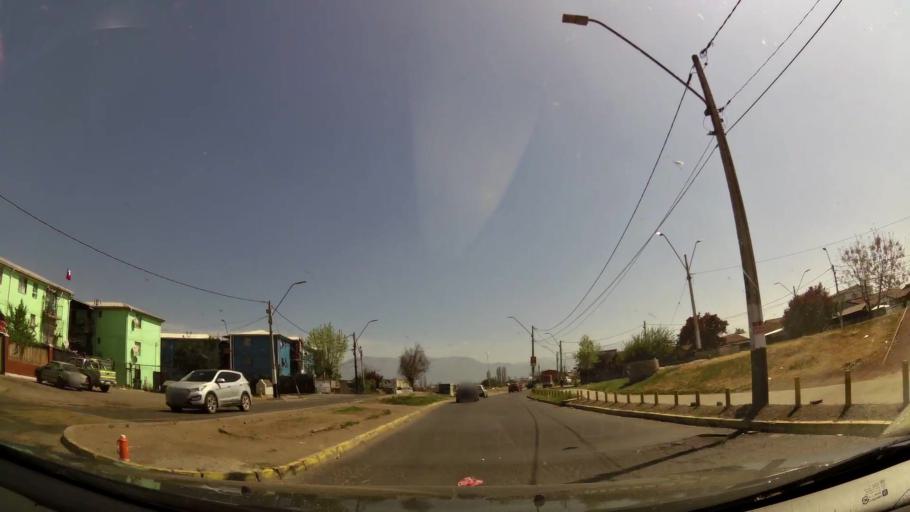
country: CL
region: Santiago Metropolitan
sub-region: Provincia de Santiago
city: Lo Prado
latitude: -33.4026
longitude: -70.7471
